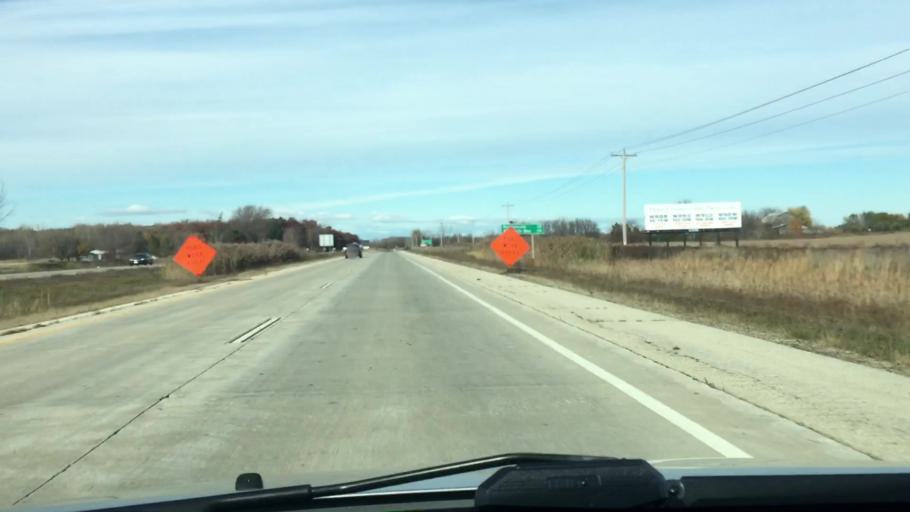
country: US
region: Wisconsin
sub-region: Brown County
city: Bellevue
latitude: 44.5492
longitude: -87.8812
